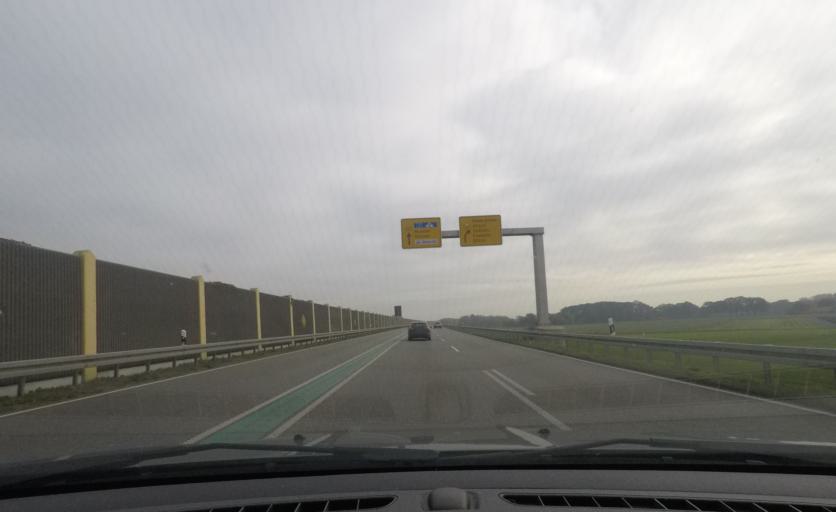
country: DE
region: North Rhine-Westphalia
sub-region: Regierungsbezirk Munster
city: Borken
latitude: 51.8296
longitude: 6.8352
